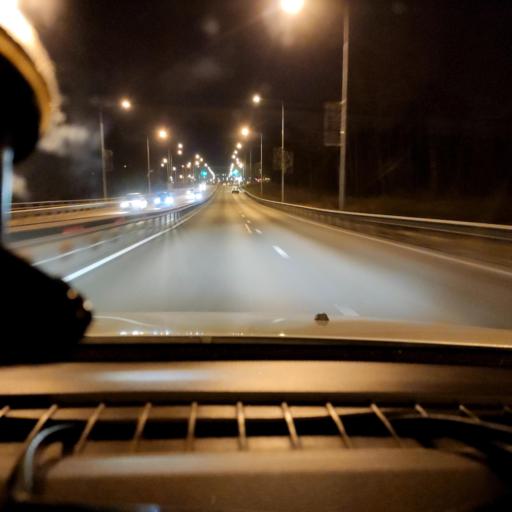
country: RU
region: Samara
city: Volzhskiy
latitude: 53.3583
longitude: 50.2073
